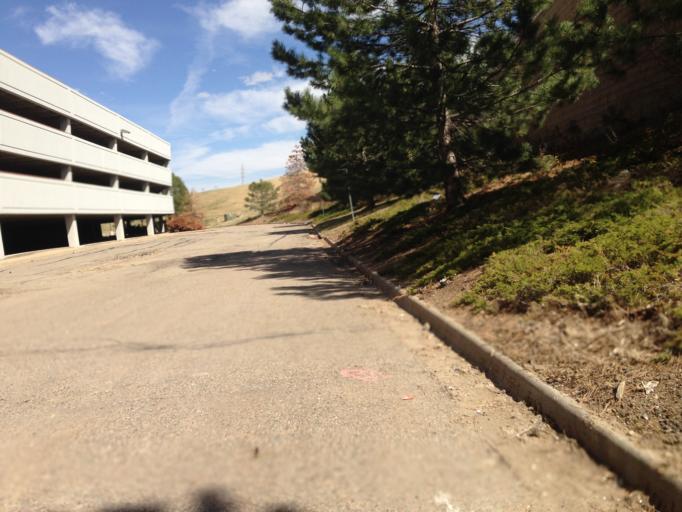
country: US
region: Colorado
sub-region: Broomfield County
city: Broomfield
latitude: 39.9292
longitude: -105.1230
